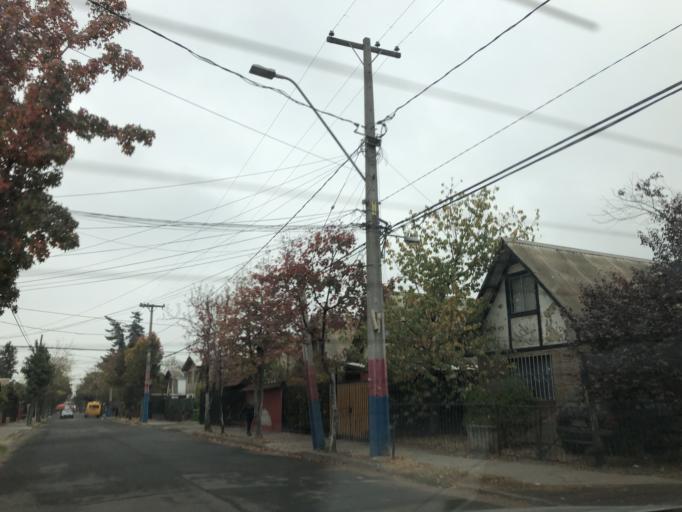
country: CL
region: Santiago Metropolitan
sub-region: Provincia de Cordillera
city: Puente Alto
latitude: -33.5905
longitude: -70.5834
